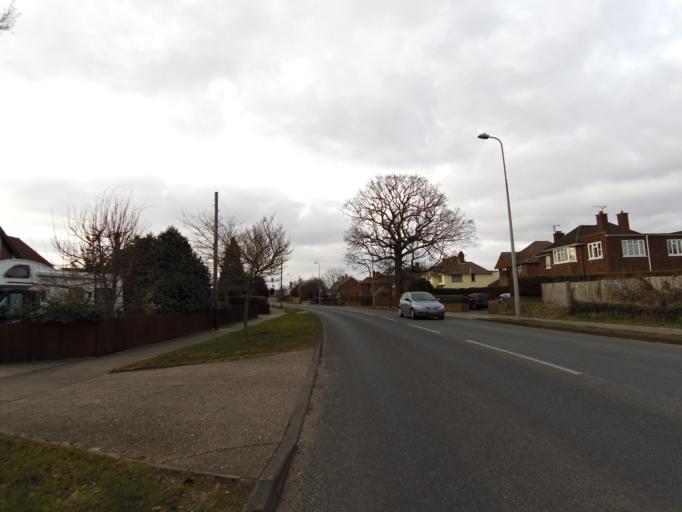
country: GB
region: England
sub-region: Suffolk
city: Ipswich
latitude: 52.0770
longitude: 1.1518
